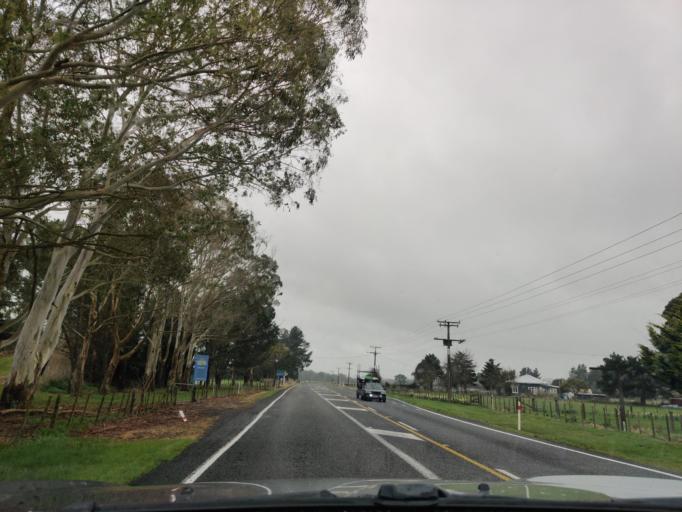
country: NZ
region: Hawke's Bay
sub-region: Hastings District
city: Hastings
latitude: -40.0214
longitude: 176.3320
